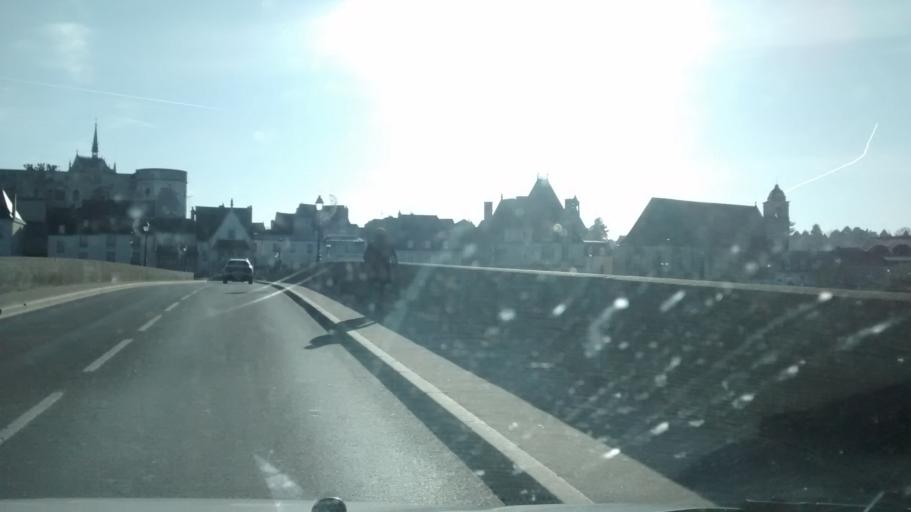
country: FR
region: Centre
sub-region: Departement d'Indre-et-Loire
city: Amboise
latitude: 47.4148
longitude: 0.9835
